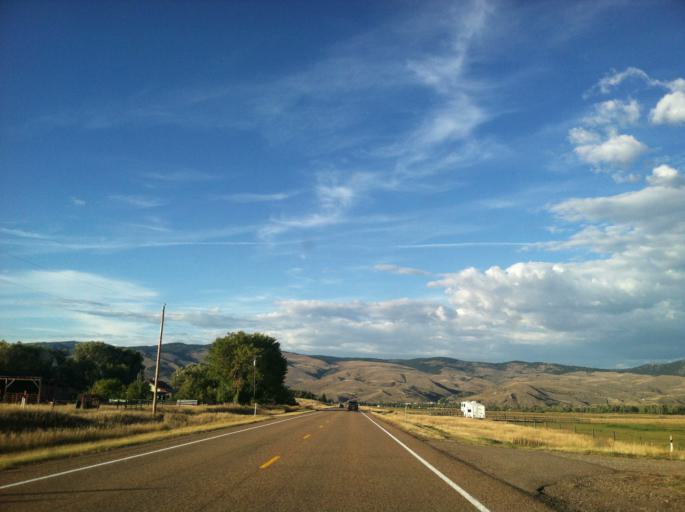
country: US
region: Montana
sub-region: Granite County
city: Philipsburg
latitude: 46.6372
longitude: -113.1681
